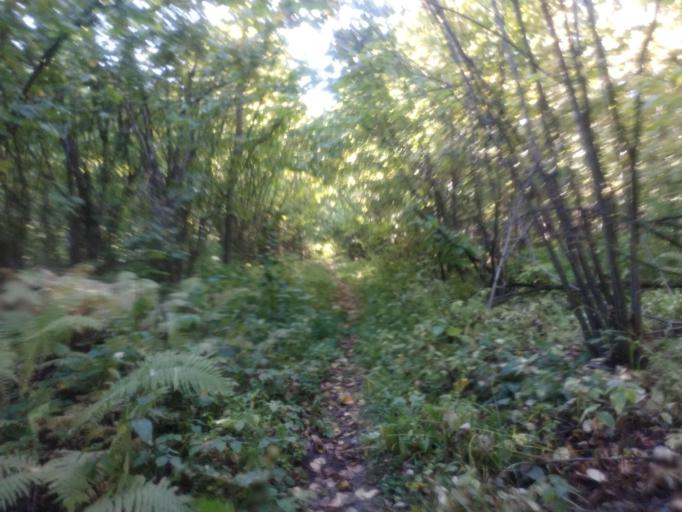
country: RU
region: Chuvashia
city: Novyye Lapsary
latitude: 56.1380
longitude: 47.1340
